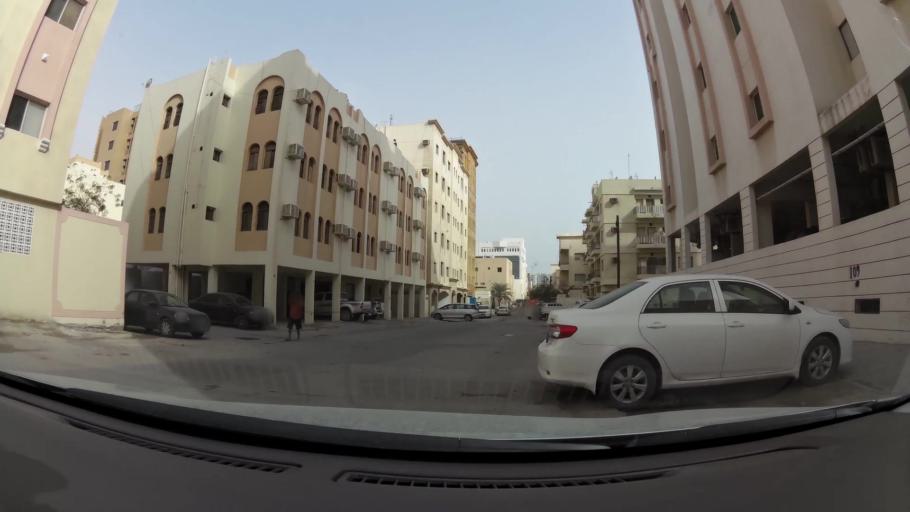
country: QA
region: Baladiyat ad Dawhah
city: Doha
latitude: 25.2792
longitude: 51.5455
